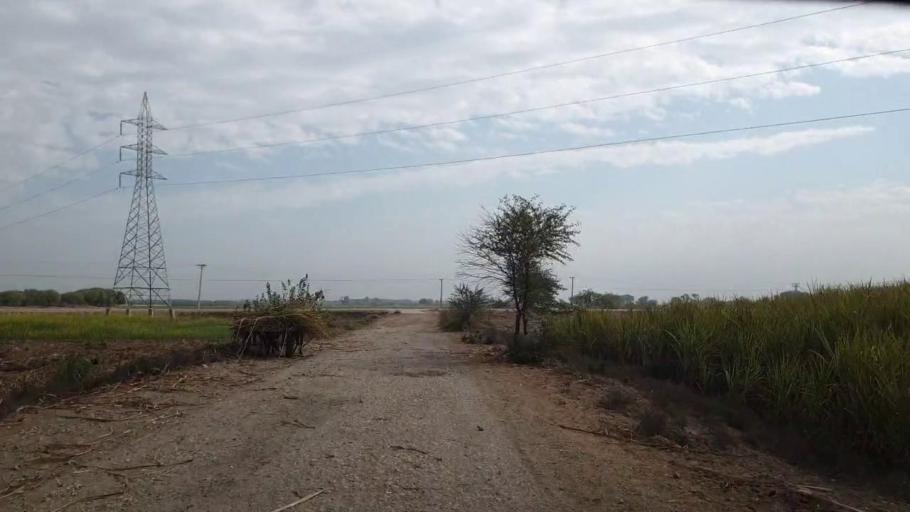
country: PK
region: Sindh
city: Matiari
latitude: 25.5720
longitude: 68.4563
